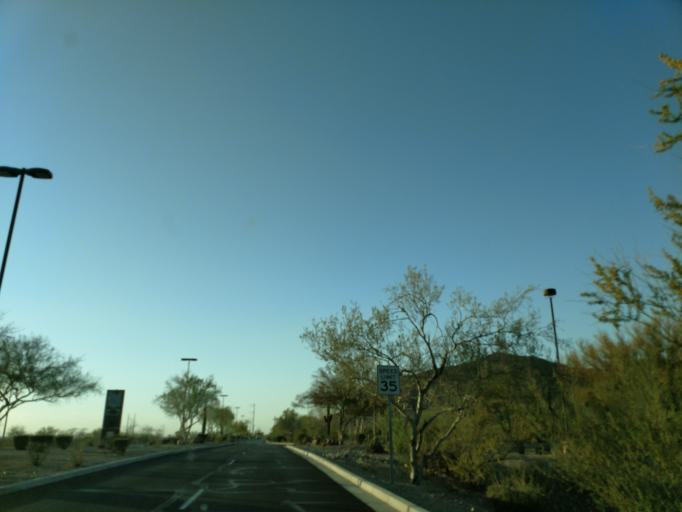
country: US
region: Arizona
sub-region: Maricopa County
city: Laveen
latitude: 33.3132
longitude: -112.1612
